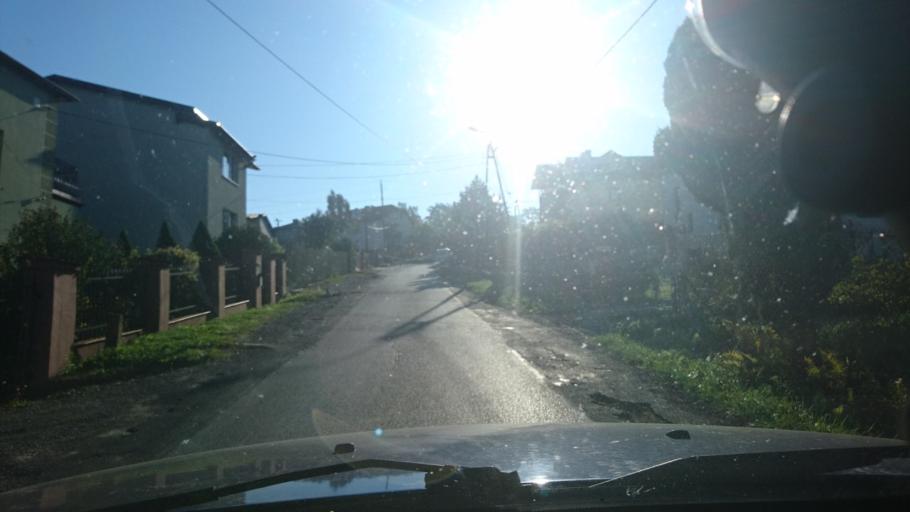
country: PL
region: Silesian Voivodeship
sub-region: Bielsko-Biala
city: Bielsko-Biala
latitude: 49.8408
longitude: 19.0765
